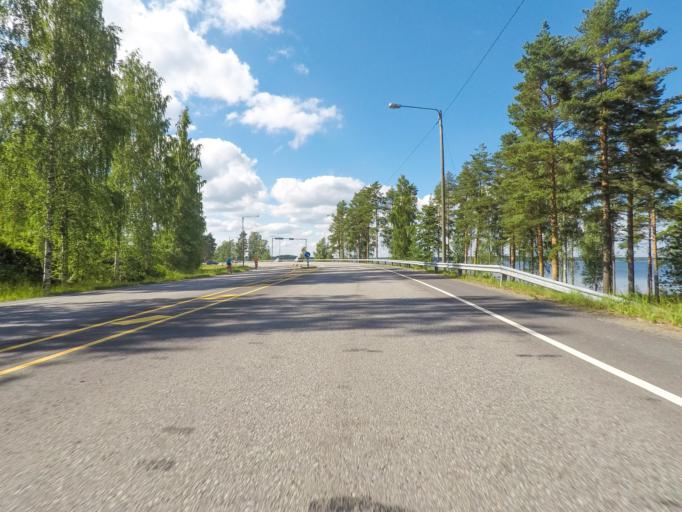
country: FI
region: Southern Savonia
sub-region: Savonlinna
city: Punkaharju
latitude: 61.8045
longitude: 29.2922
